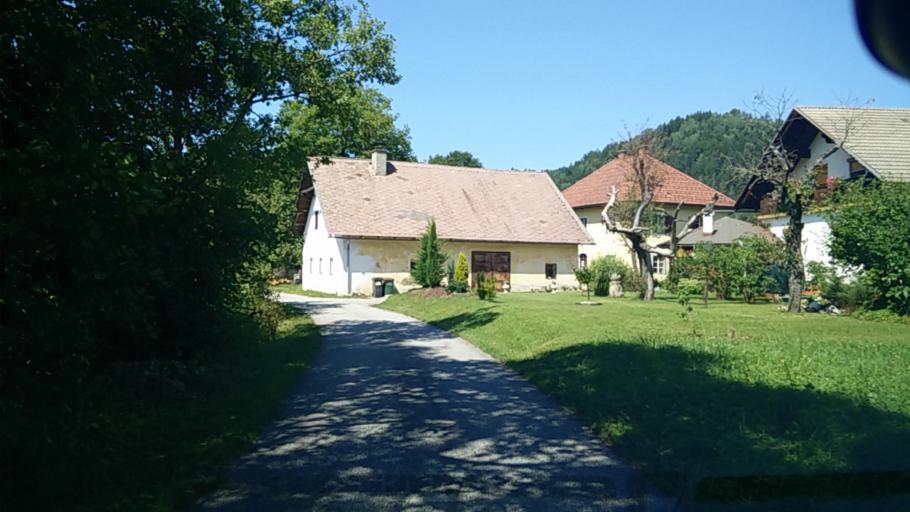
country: AT
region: Carinthia
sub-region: Politischer Bezirk Volkermarkt
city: Sittersdorf
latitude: 46.5433
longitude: 14.5903
